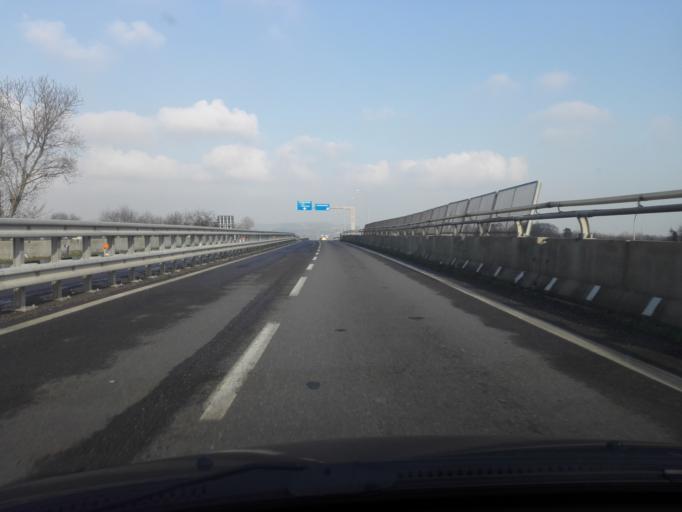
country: IT
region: Piedmont
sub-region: Provincia di Alessandria
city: Alessandria
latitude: 44.9071
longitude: 8.6408
